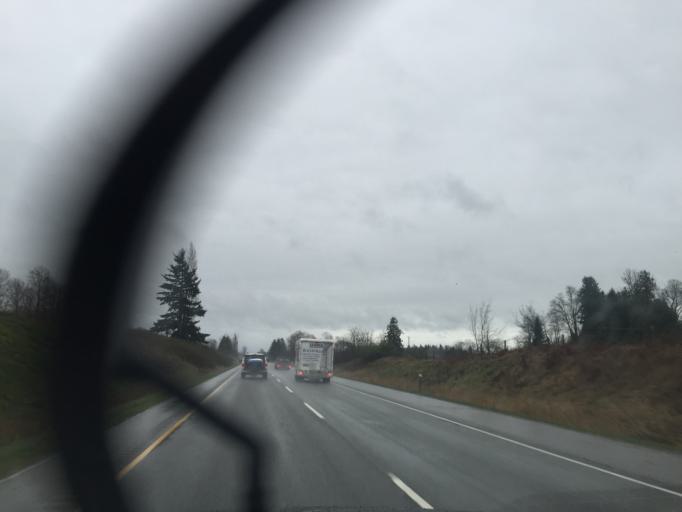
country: CA
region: British Columbia
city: Aldergrove
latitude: 49.0913
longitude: -122.4671
